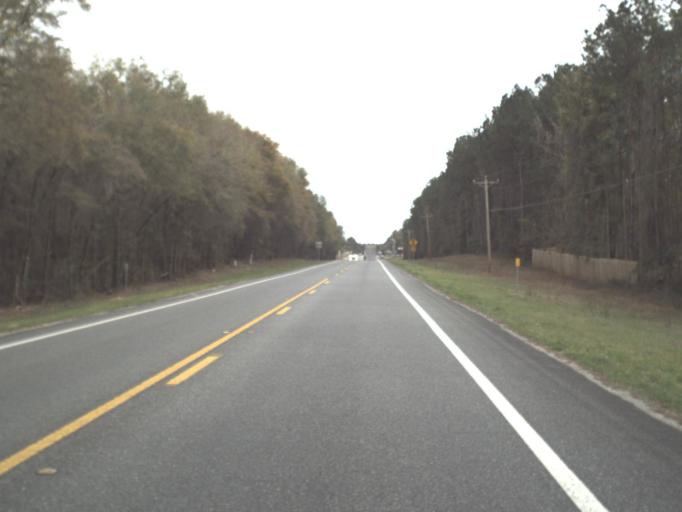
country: US
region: Florida
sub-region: Wakulla County
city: Crawfordville
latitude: 30.2663
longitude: -84.3669
